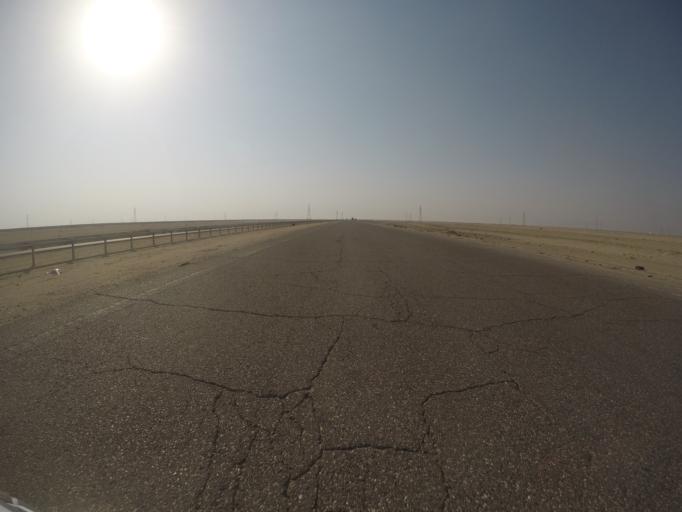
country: IQ
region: Basra Governorate
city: Az Zubayr
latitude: 30.4606
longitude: 47.3700
